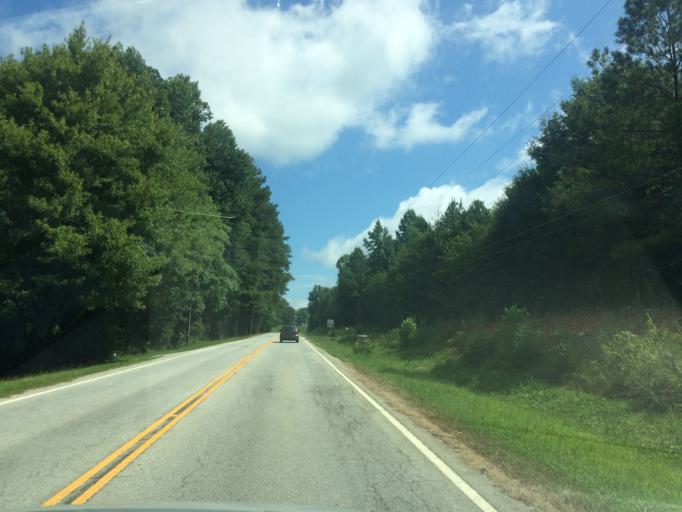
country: US
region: South Carolina
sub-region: Spartanburg County
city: Inman
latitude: 35.0571
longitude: -82.0834
